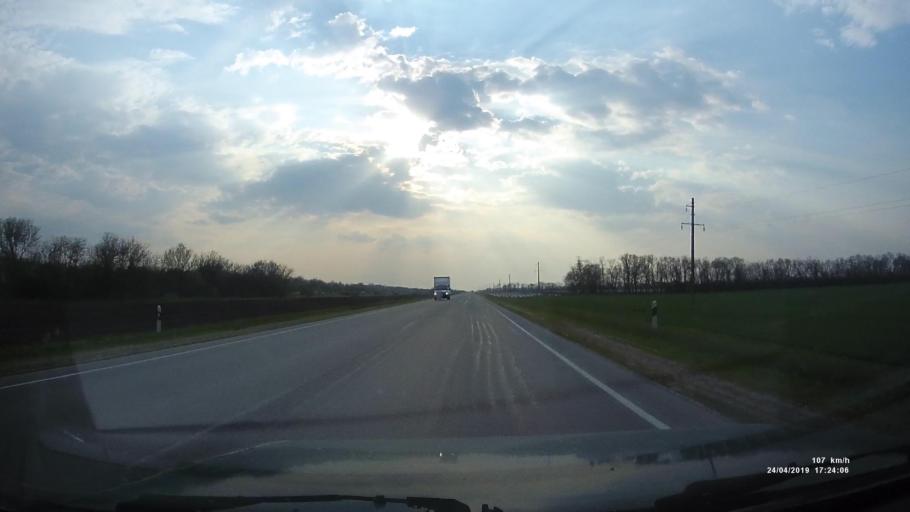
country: RU
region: Rostov
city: Gigant
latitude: 46.5228
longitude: 41.2702
